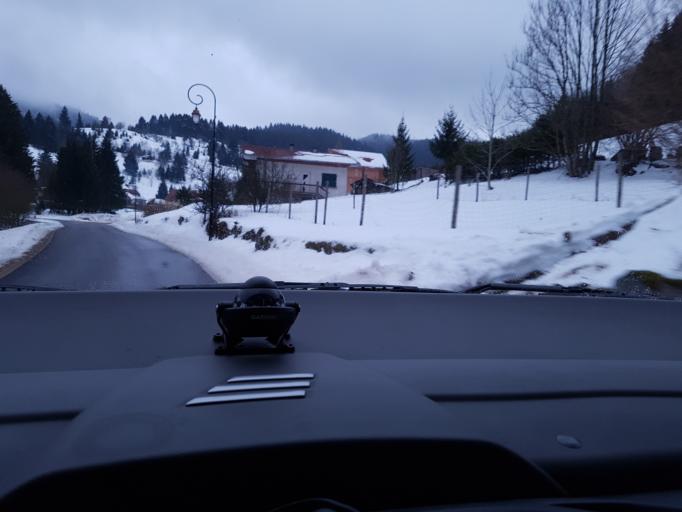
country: FR
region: Lorraine
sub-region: Departement des Vosges
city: Plainfaing
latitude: 48.1009
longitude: 7.0240
